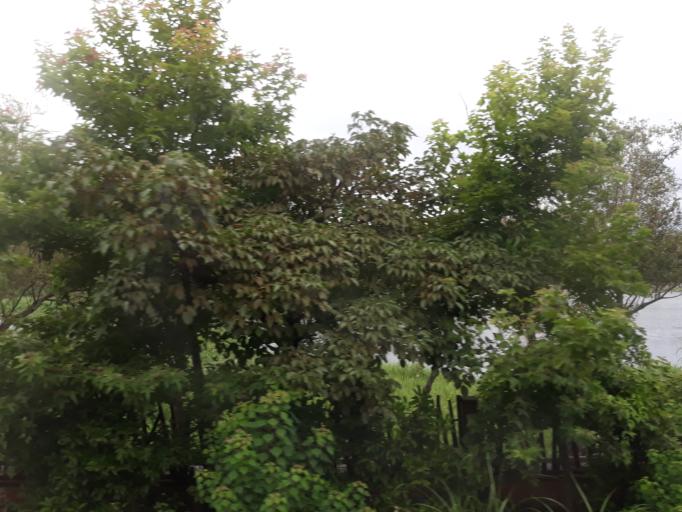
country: TW
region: Taiwan
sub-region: Yilan
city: Yilan
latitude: 24.6833
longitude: 121.7747
